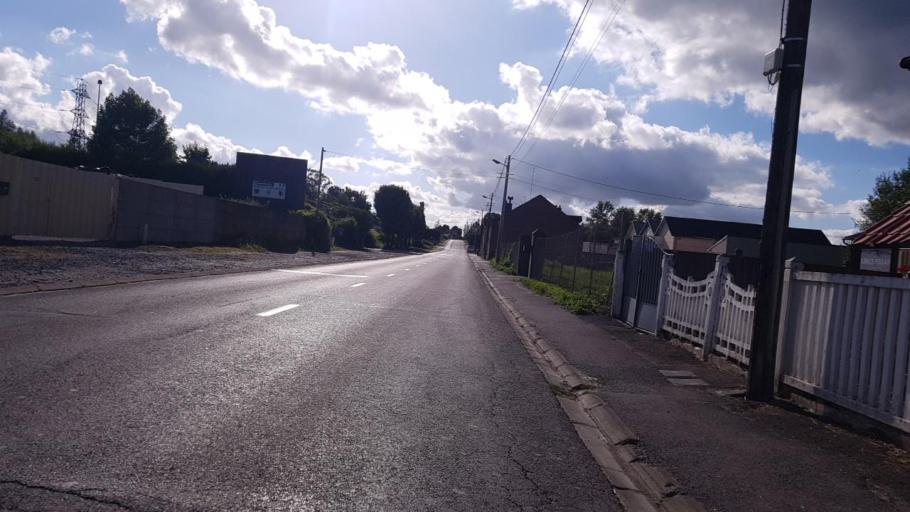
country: FR
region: Picardie
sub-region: Departement de l'Aisne
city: Hirson
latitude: 49.9208
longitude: 4.0725
